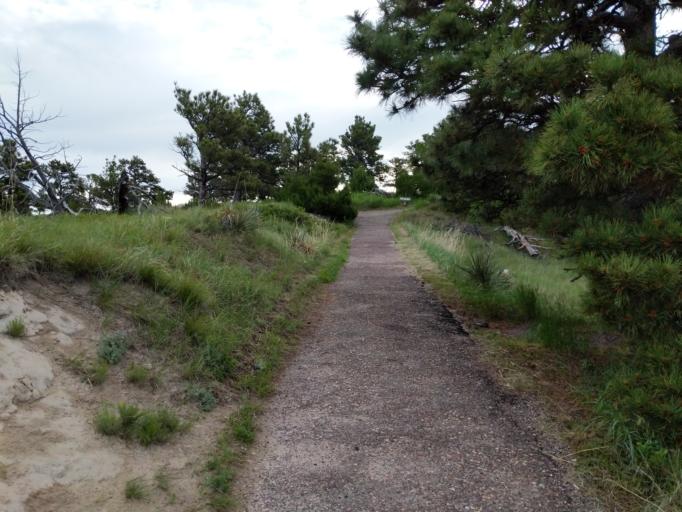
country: US
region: Nebraska
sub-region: Scotts Bluff County
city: Terrytown
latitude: 41.8376
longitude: -103.6997
